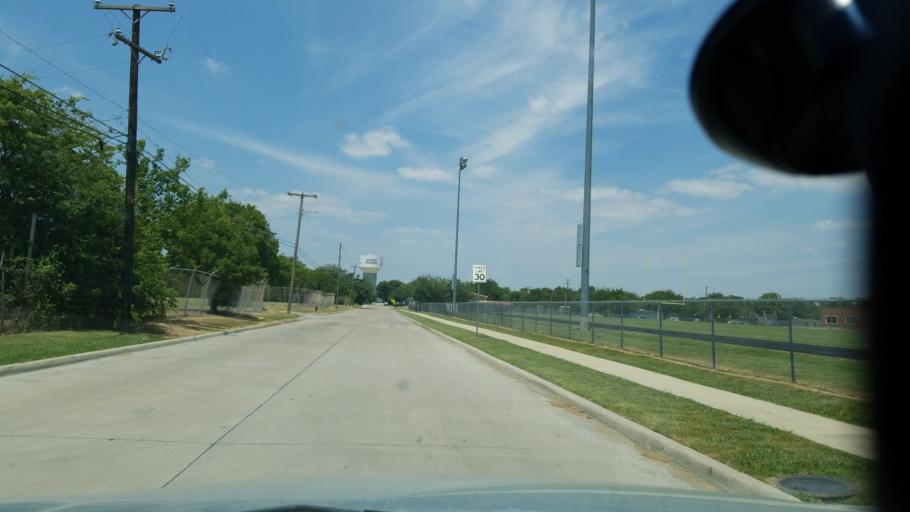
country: US
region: Texas
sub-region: Dallas County
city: Grand Prairie
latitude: 32.7511
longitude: -96.9660
